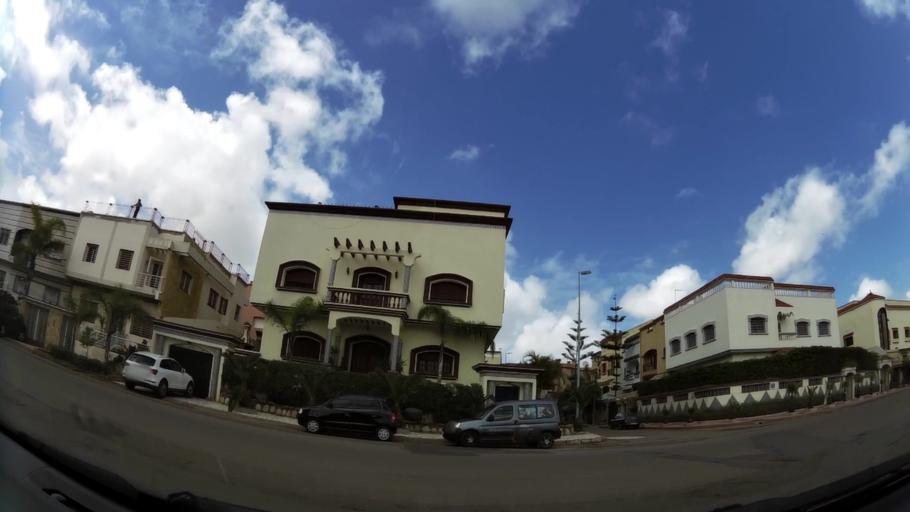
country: MA
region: Grand Casablanca
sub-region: Casablanca
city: Casablanca
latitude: 33.5305
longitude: -7.6006
